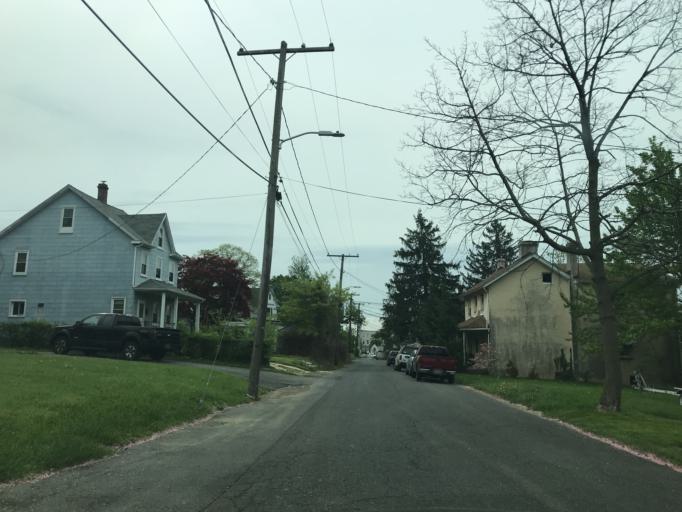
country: US
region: Maryland
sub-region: Baltimore County
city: Catonsville
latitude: 39.2736
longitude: -76.7351
